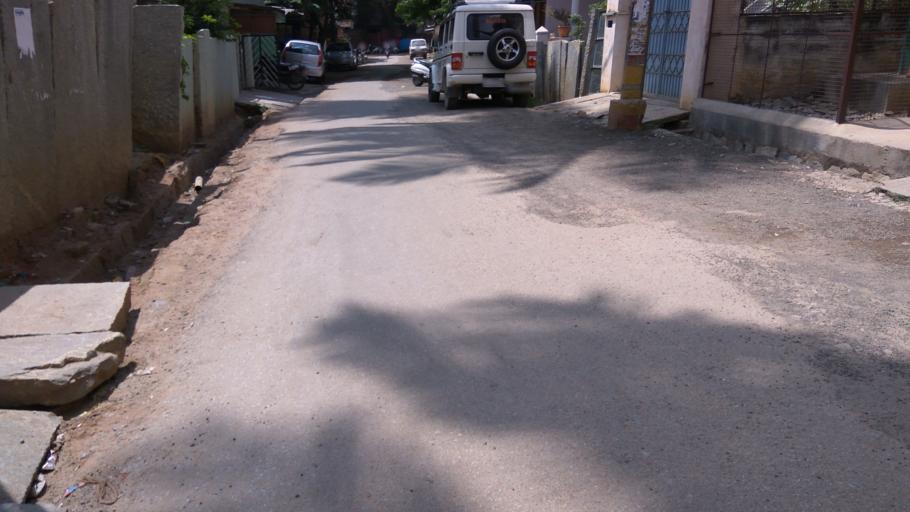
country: IN
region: Karnataka
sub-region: Bangalore Urban
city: Bangalore
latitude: 12.9665
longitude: 77.6401
